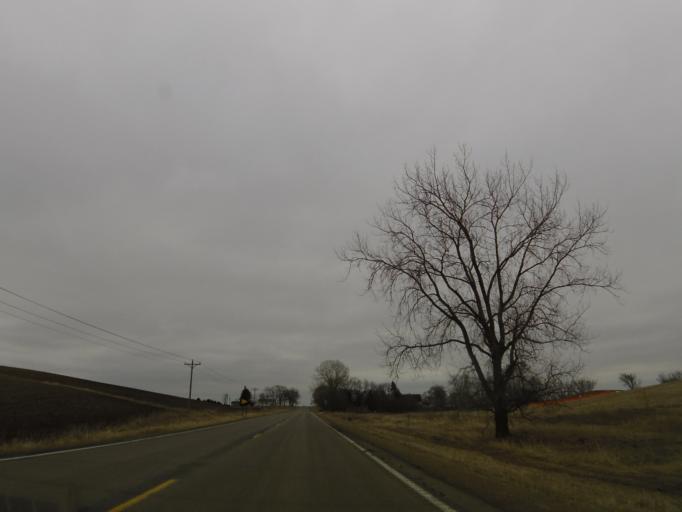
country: US
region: Minnesota
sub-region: Scott County
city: Prior Lake
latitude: 44.6742
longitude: -93.3845
